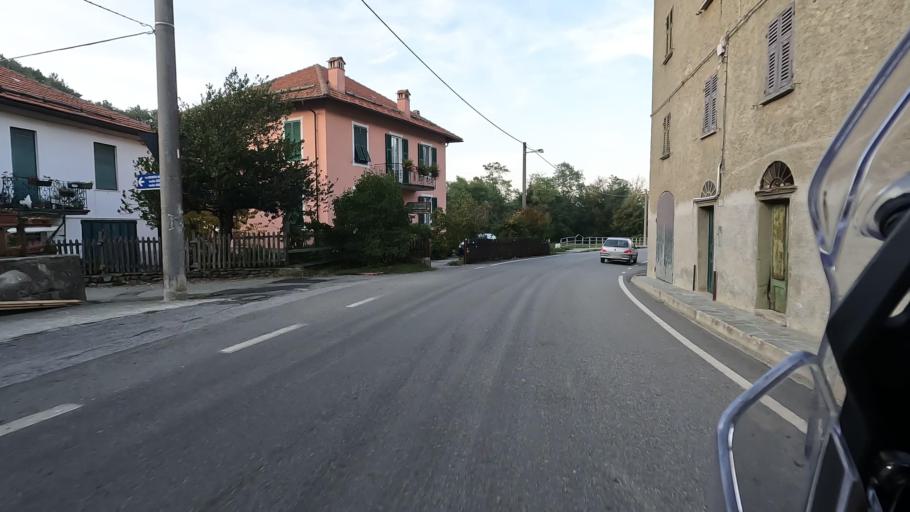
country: IT
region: Liguria
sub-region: Provincia di Savona
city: Sassello
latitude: 44.4709
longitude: 8.4843
